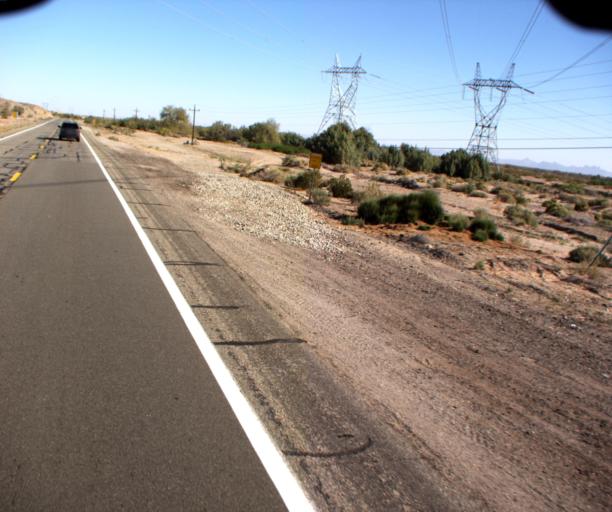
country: US
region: Arizona
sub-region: Yuma County
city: Fortuna Foothills
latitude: 32.7883
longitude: -114.3813
